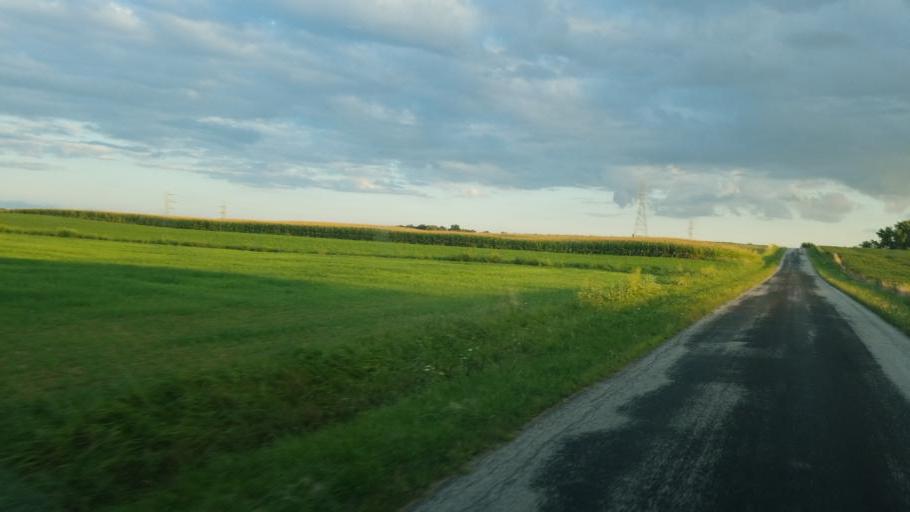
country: US
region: Ohio
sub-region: Richland County
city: Lincoln Heights
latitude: 40.8564
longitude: -82.5328
